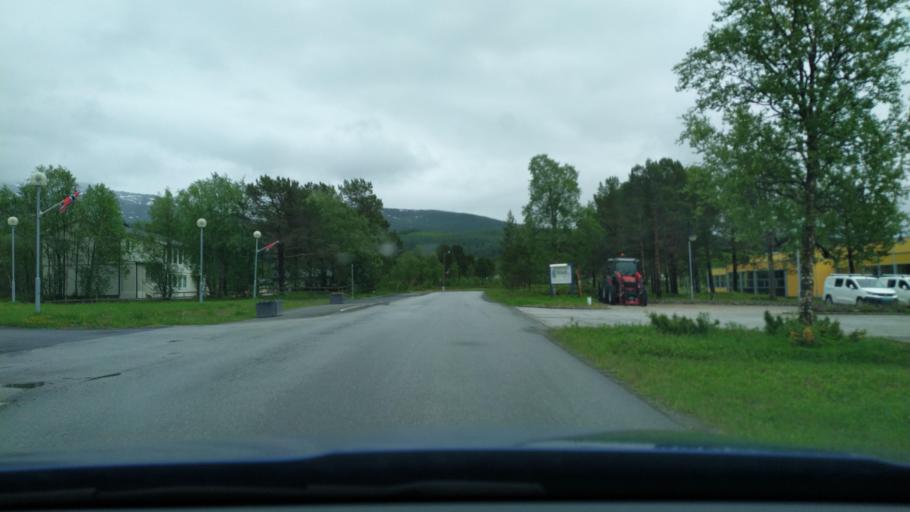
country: NO
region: Troms
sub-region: Dyroy
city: Brostadbotn
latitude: 69.0908
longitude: 17.6979
